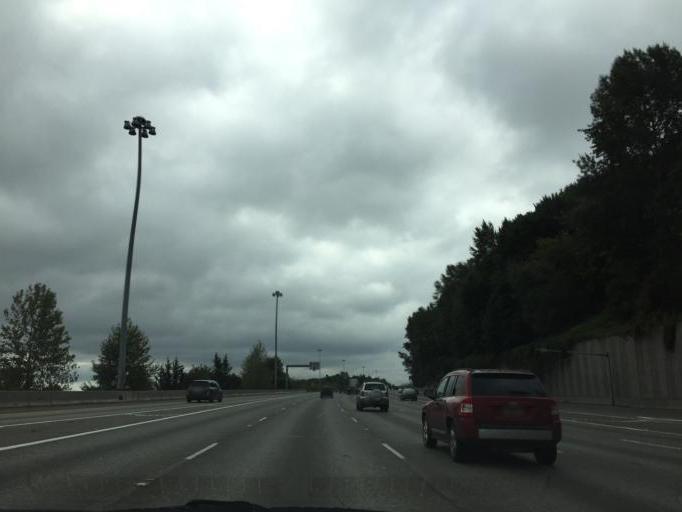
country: US
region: Washington
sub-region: King County
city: Tukwila
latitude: 47.4562
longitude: -122.2642
